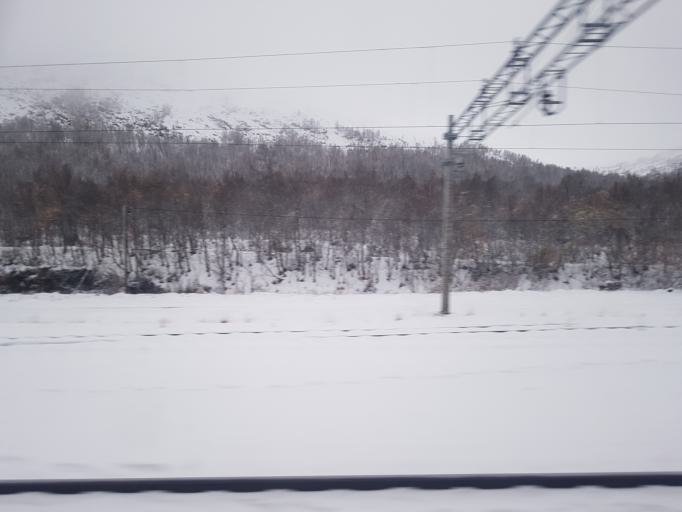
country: NO
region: Oppland
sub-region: Dovre
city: Dovre
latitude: 62.2310
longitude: 9.5389
